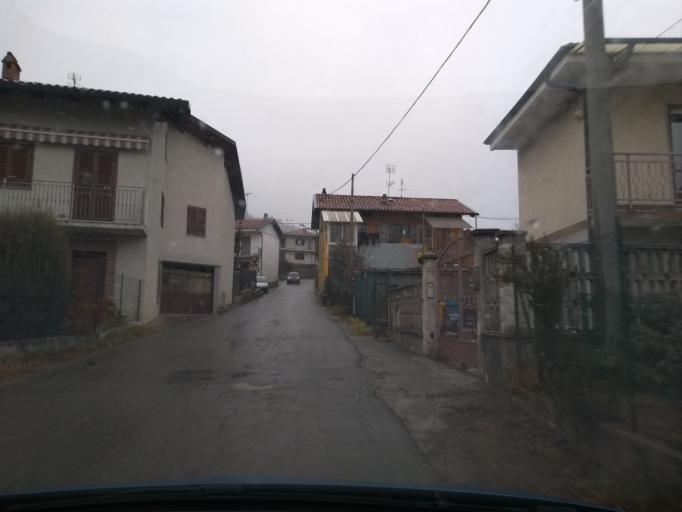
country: IT
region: Piedmont
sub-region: Provincia di Torino
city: Chiesanuova
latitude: 45.4052
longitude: 7.6600
